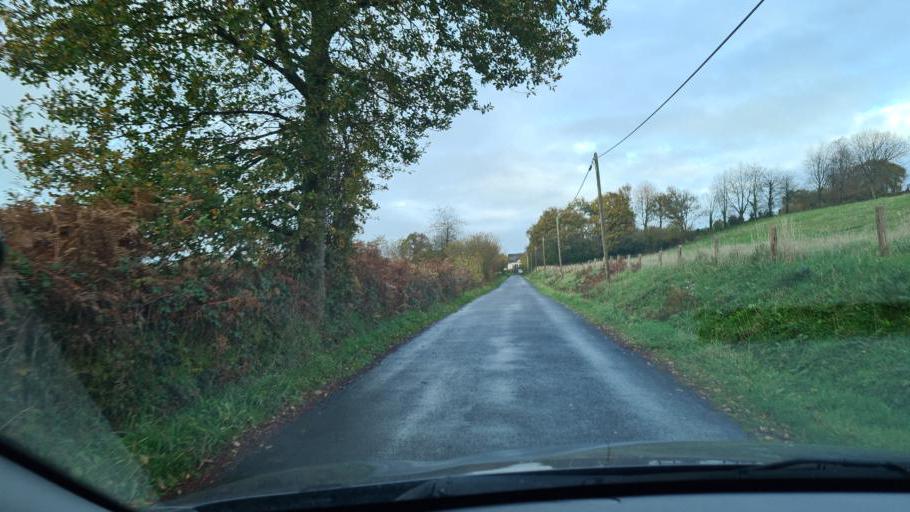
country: FR
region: Lower Normandy
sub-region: Departement de la Manche
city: La Haye-Pesnel
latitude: 48.7888
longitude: -1.3975
